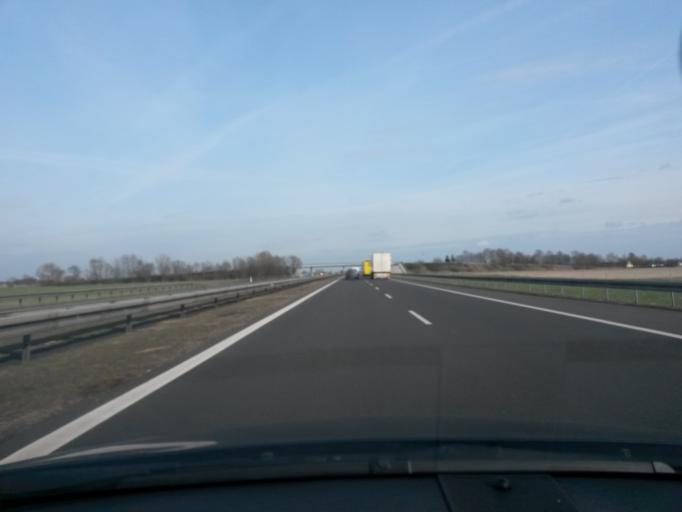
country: PL
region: Greater Poland Voivodeship
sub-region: Powiat koninski
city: Rzgow Pierwszy
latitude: 52.2086
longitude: 18.0051
